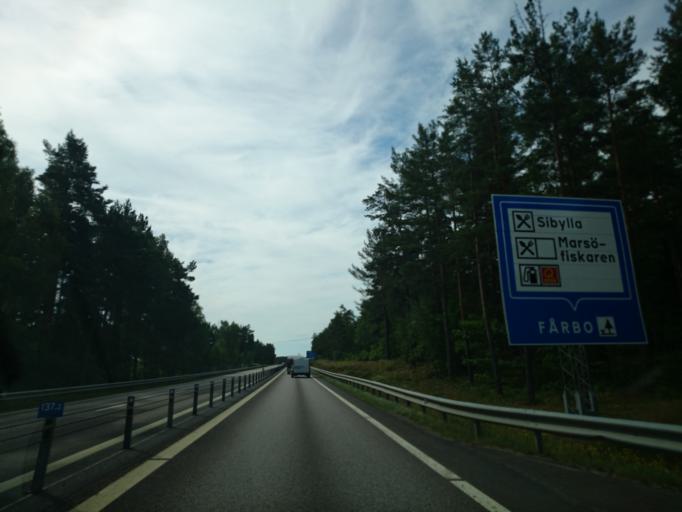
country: SE
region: Kalmar
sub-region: Oskarshamns Kommun
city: Oskarshamn
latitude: 57.3881
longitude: 16.4794
